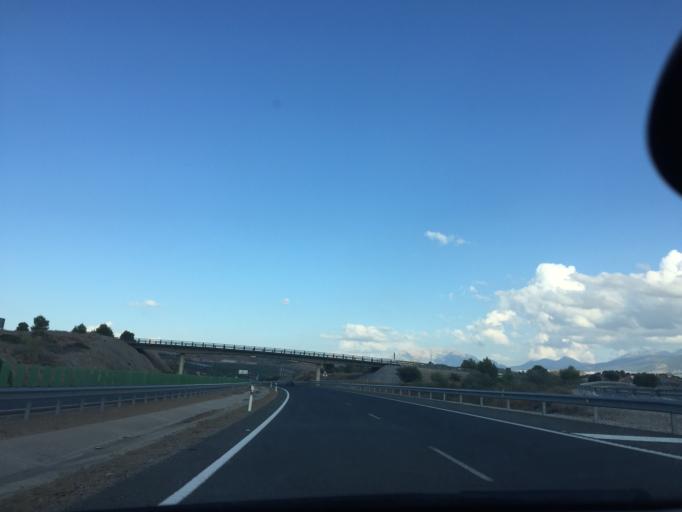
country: ES
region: Andalusia
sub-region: Provincia de Jaen
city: La Guardia de Jaen
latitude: 37.8018
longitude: -3.7202
